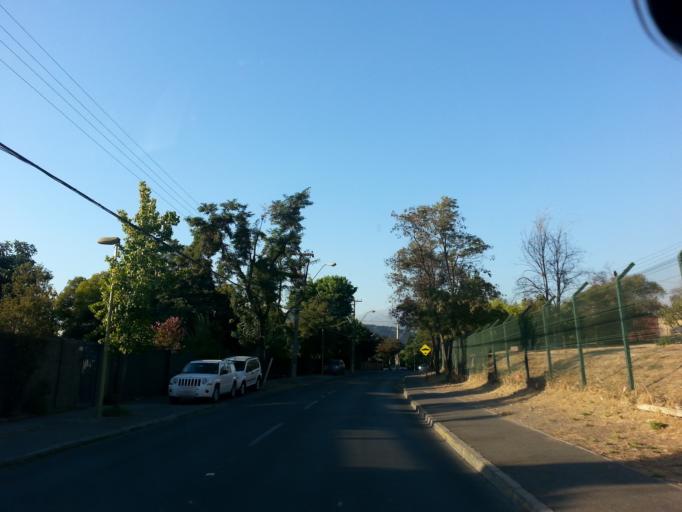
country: CL
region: Santiago Metropolitan
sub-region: Provincia de Santiago
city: Villa Presidente Frei, Nunoa, Santiago, Chile
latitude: -33.3947
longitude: -70.5398
